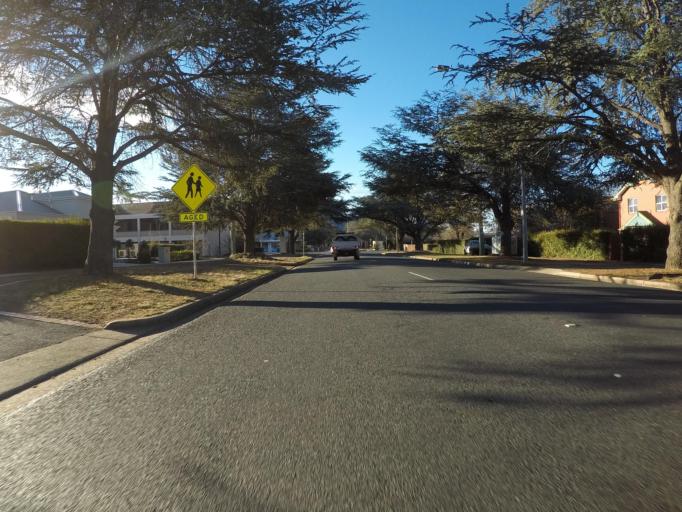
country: AU
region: Australian Capital Territory
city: Forrest
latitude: -35.3085
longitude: 149.0982
